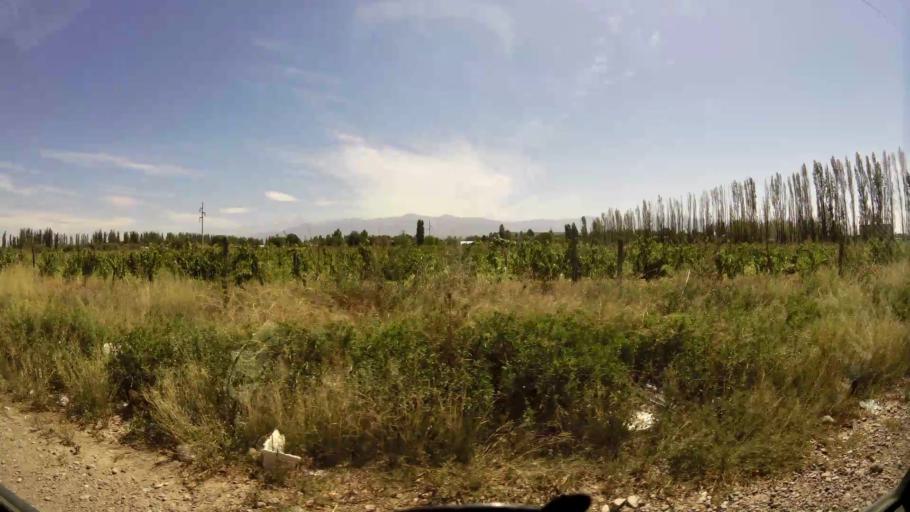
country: AR
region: Mendoza
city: Lujan de Cuyo
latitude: -32.9873
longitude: -68.8511
